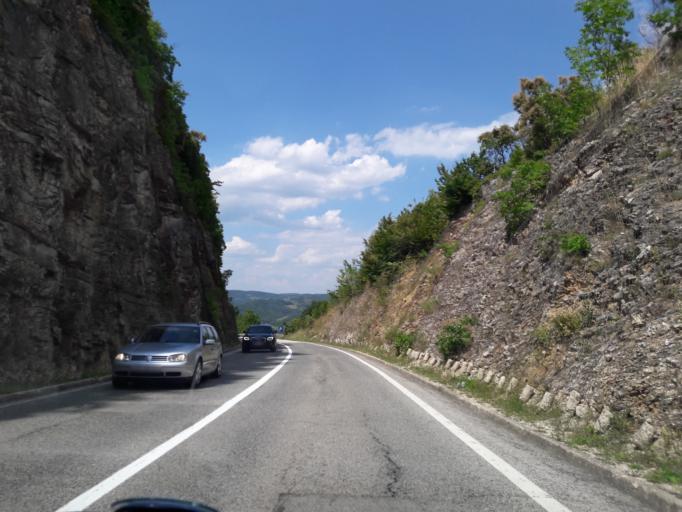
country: BA
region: Republika Srpska
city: Mrkonjic Grad
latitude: 44.5120
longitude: 17.1532
